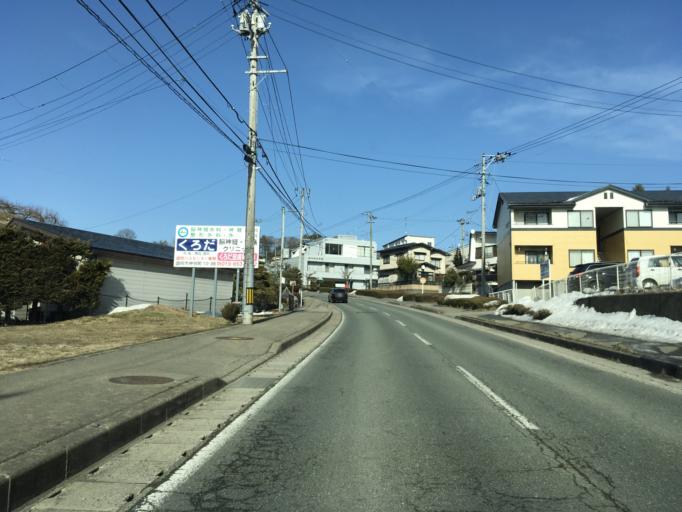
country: JP
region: Iwate
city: Morioka-shi
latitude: 39.7210
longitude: 141.1561
